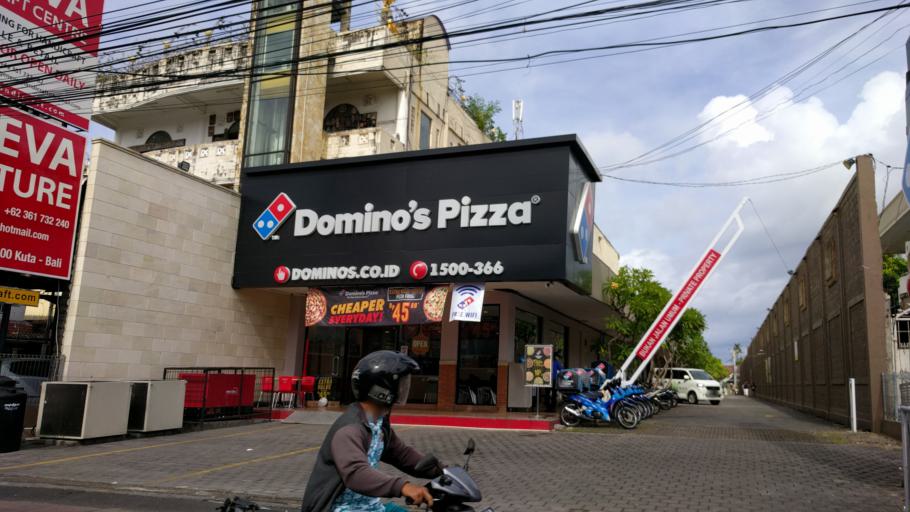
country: ID
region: Bali
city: Kuta
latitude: -8.6795
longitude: 115.1645
